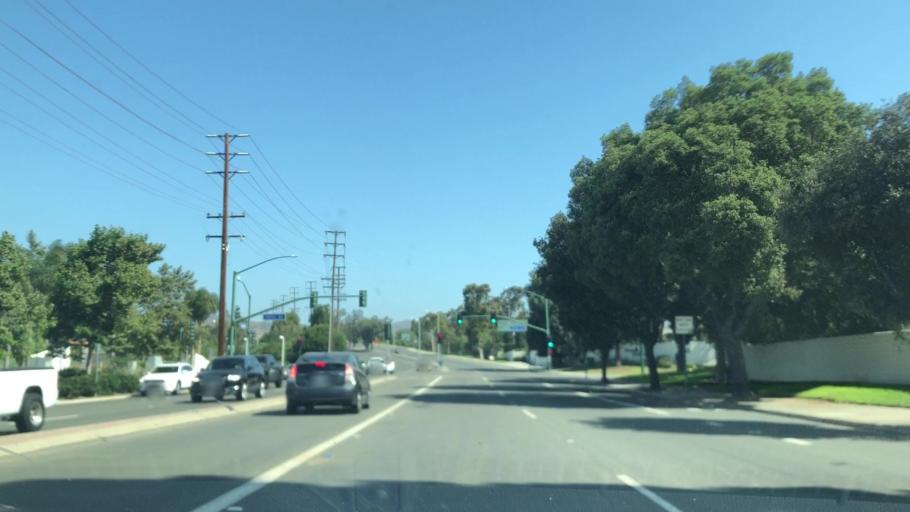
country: US
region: California
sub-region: Ventura County
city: Saticoy
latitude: 34.2704
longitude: -119.1889
